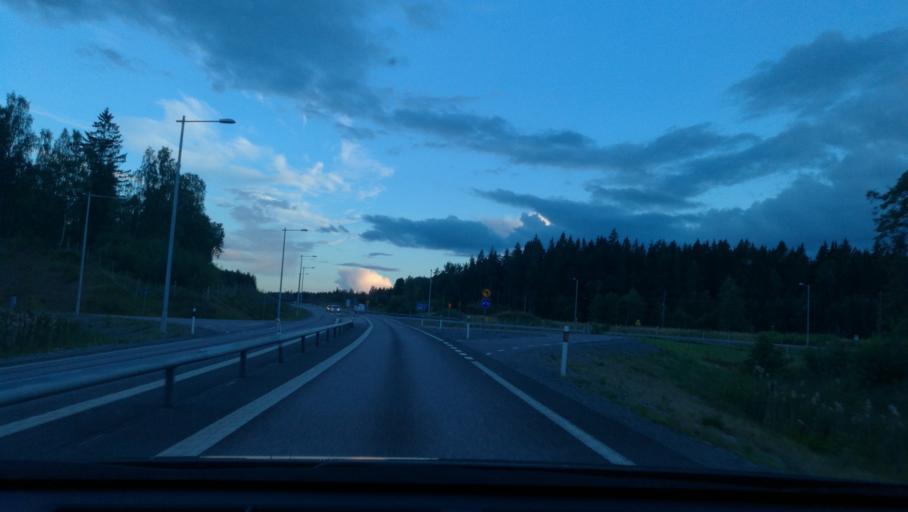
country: SE
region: Soedermanland
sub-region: Katrineholms Kommun
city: Katrineholm
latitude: 58.9322
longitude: 16.1964
